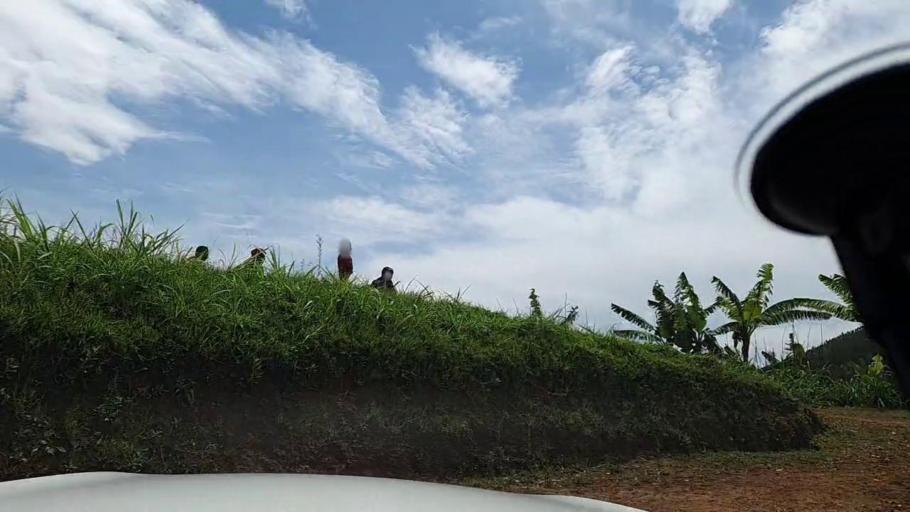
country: RW
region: Southern Province
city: Gitarama
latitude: -2.0773
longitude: 29.6694
